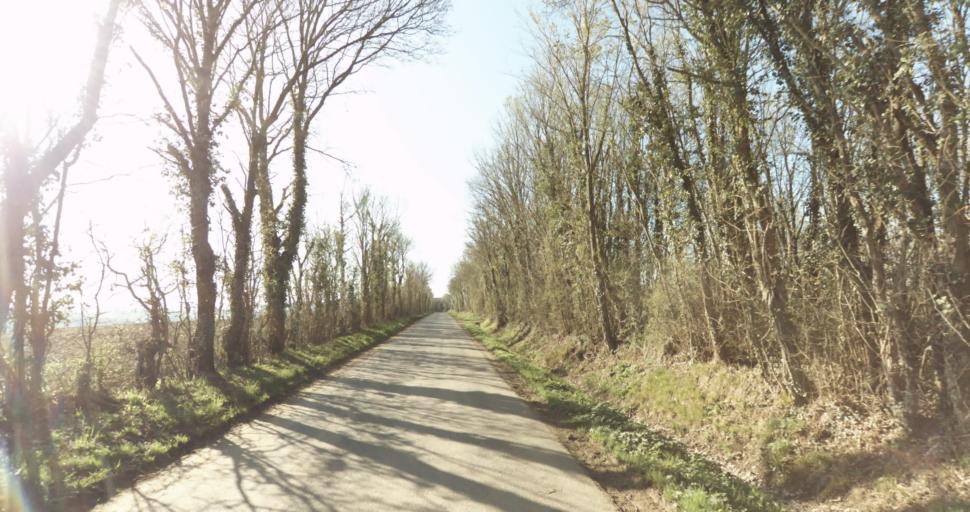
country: FR
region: Lower Normandy
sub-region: Departement du Calvados
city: Saint-Pierre-sur-Dives
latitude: 48.9955
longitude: -0.0027
